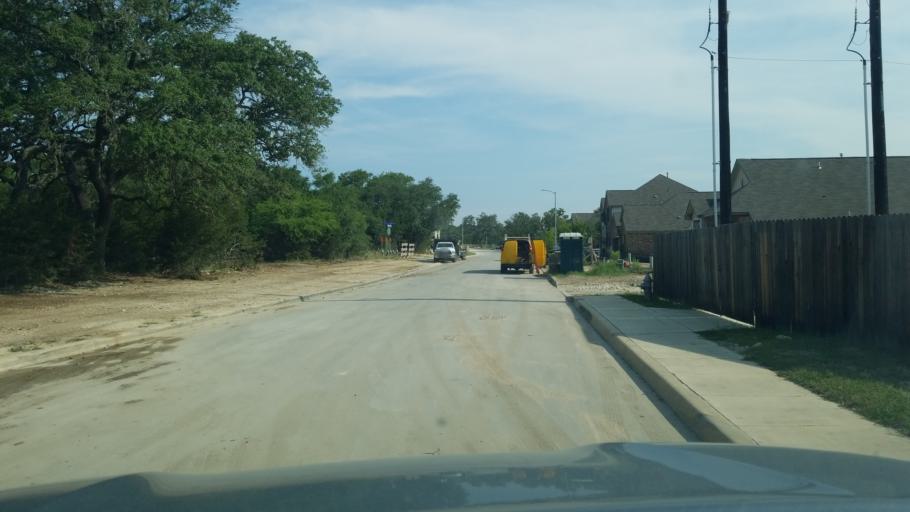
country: US
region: Texas
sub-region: Bexar County
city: Scenic Oaks
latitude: 29.7113
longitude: -98.6524
